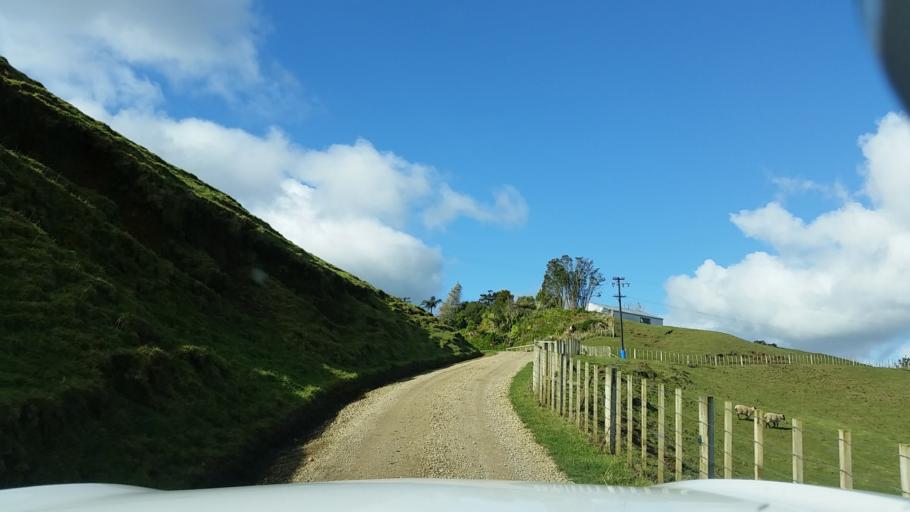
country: NZ
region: Taranaki
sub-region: South Taranaki District
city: Patea
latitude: -39.6699
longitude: 174.5659
